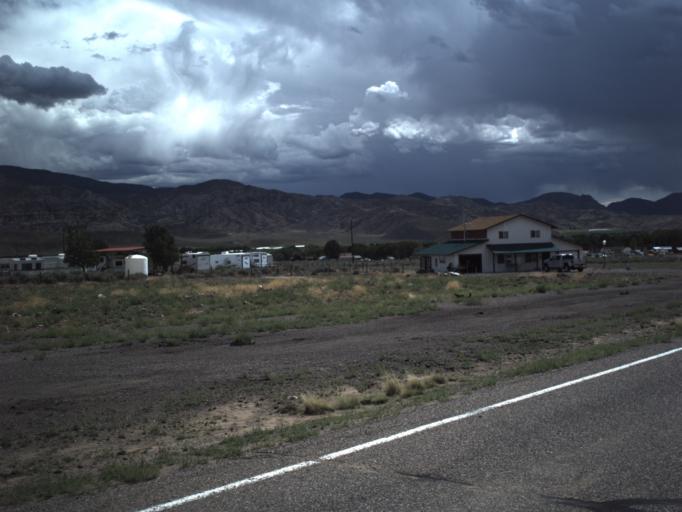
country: US
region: Utah
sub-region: Piute County
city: Junction
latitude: 38.2438
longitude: -112.2326
